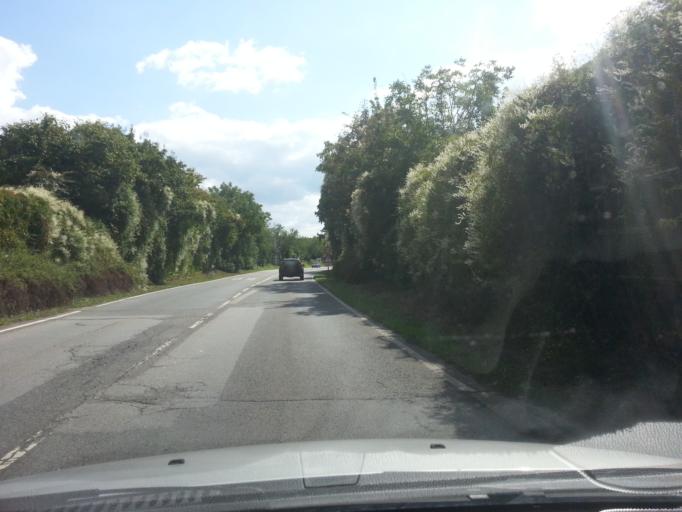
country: DE
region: Baden-Wuerttemberg
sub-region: Karlsruhe Region
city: Wiesloch
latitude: 49.2902
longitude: 8.7022
